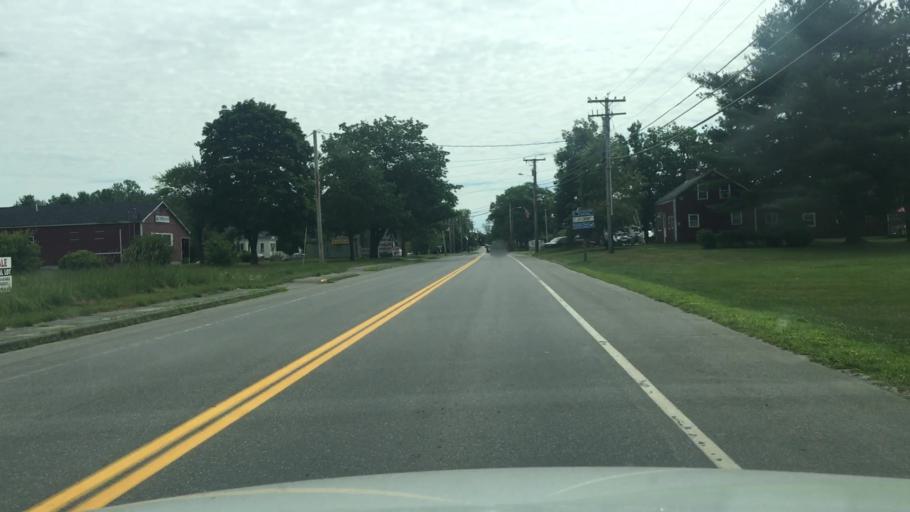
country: US
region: Maine
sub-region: Waldo County
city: Troy
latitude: 44.6122
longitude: -69.3405
